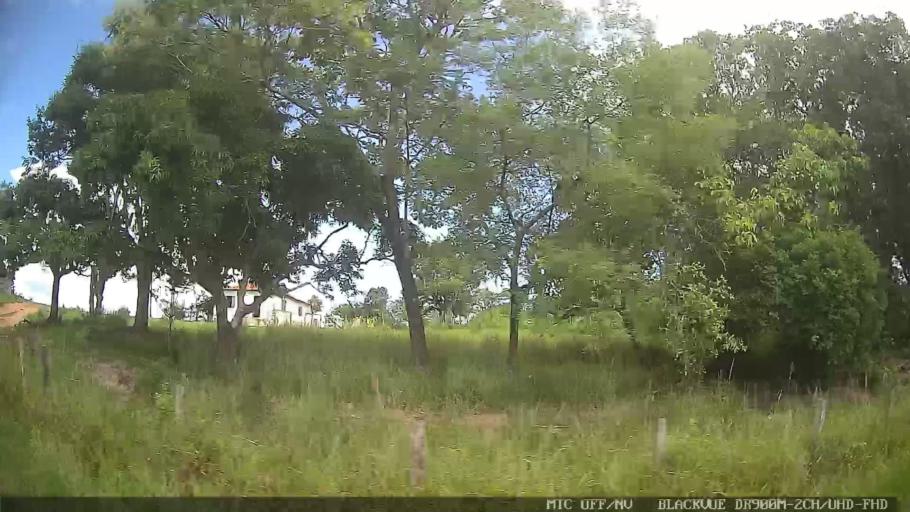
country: BR
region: Sao Paulo
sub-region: Conchas
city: Conchas
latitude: -22.9956
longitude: -47.9995
